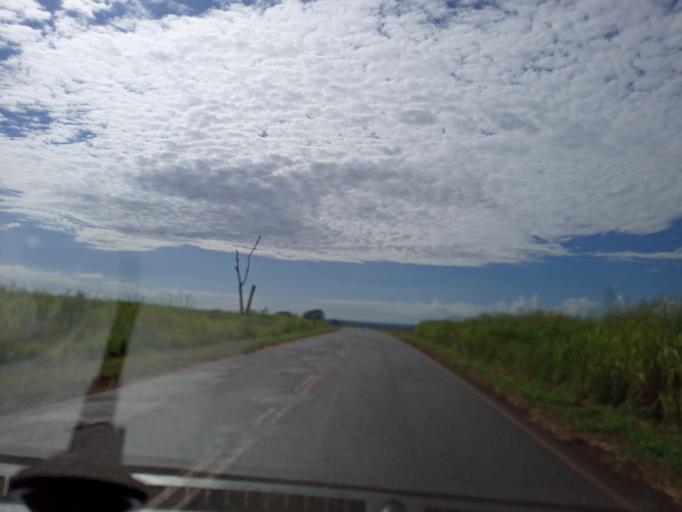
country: BR
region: Goias
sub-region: Itumbiara
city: Itumbiara
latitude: -18.4657
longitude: -49.1269
